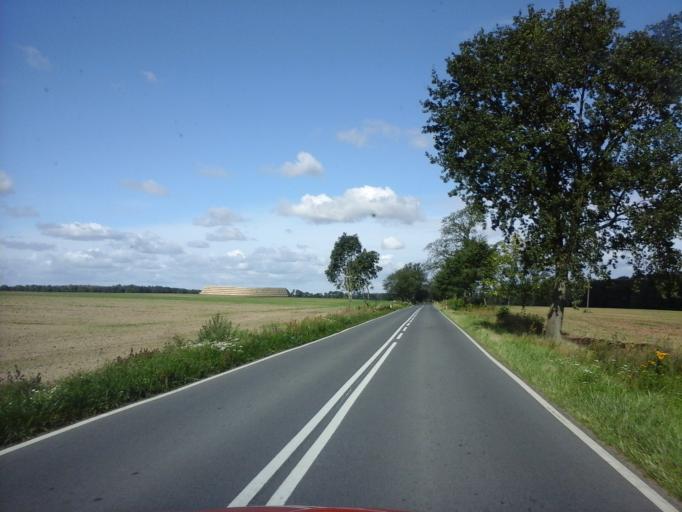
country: PL
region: West Pomeranian Voivodeship
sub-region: Powiat stargardzki
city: Dolice
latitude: 53.2002
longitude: 15.1665
